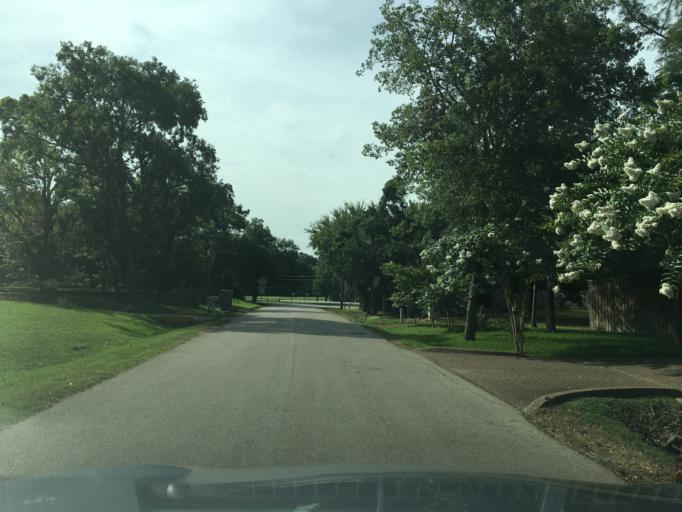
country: US
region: Texas
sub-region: Dallas County
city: Addison
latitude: 32.9283
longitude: -96.7842
